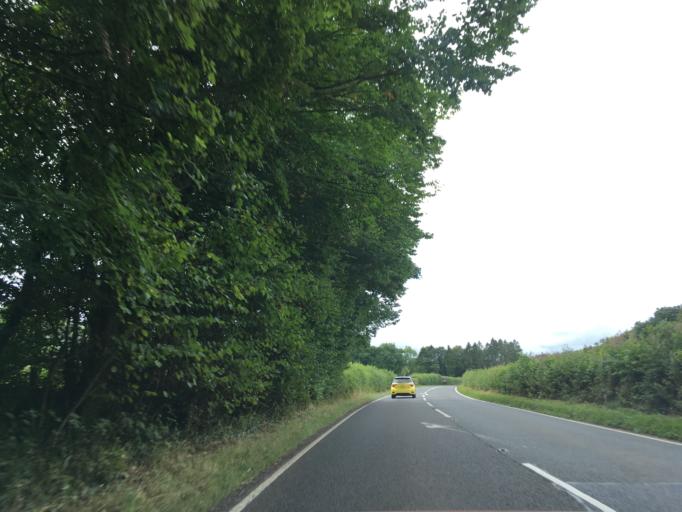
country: GB
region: Wales
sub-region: Sir Powys
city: Cray
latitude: 51.9437
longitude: -3.5796
